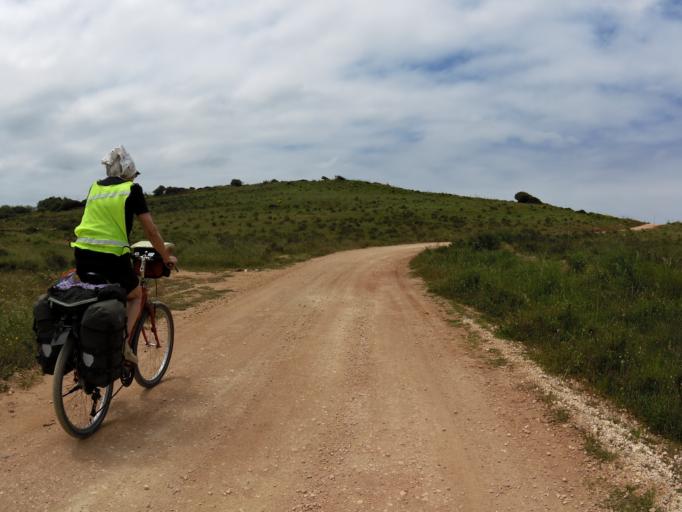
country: PT
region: Faro
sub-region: Vila do Bispo
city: Vila do Bispo
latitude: 37.0877
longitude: -8.8987
